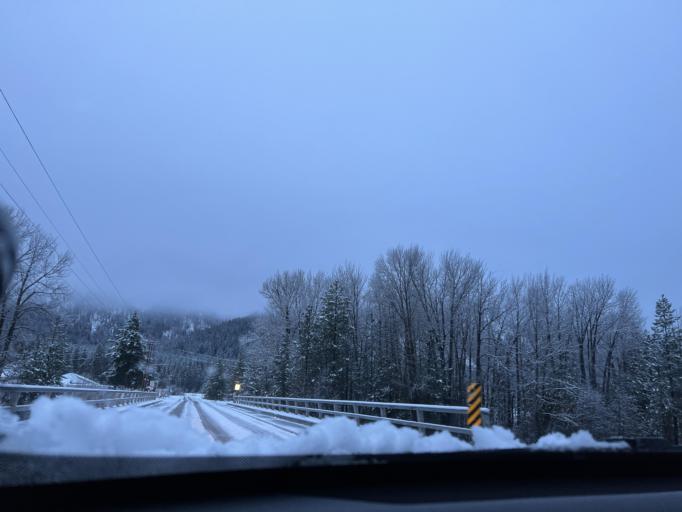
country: US
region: Washington
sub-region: Chelan County
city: Granite Falls
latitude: 48.5905
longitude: -120.4067
